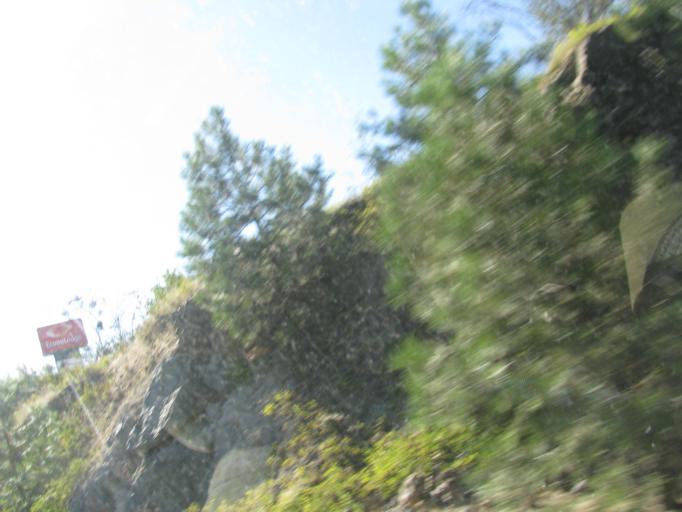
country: US
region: Washington
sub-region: Spokane County
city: Spokane
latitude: 47.6410
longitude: -117.4705
